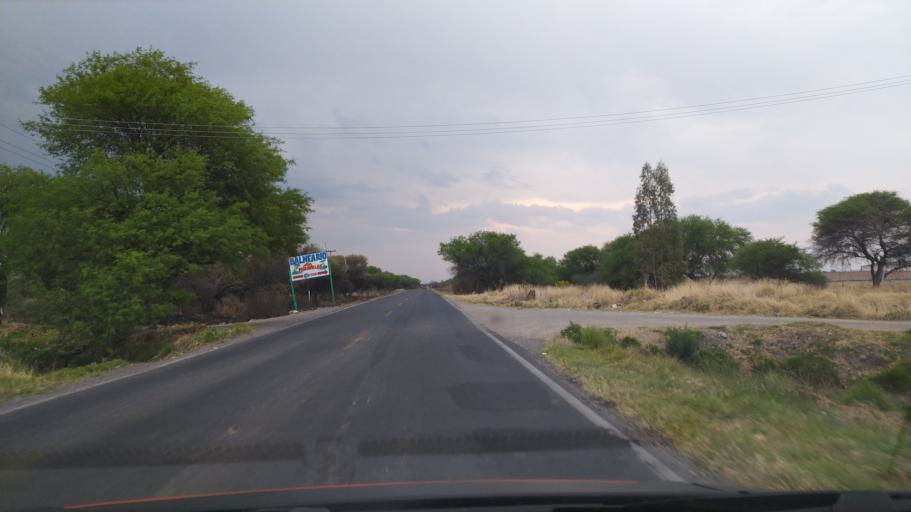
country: MX
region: Guanajuato
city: Ciudad Manuel Doblado
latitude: 20.7643
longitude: -101.9151
